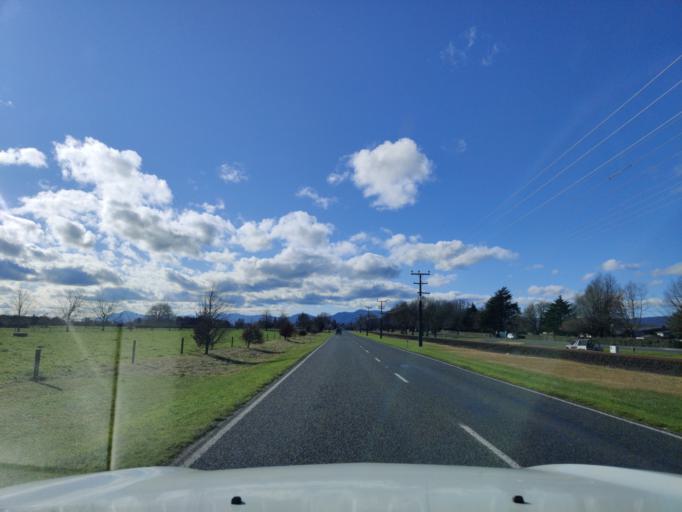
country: NZ
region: Waikato
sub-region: Matamata-Piako District
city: Matamata
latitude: -37.8341
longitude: 175.7661
